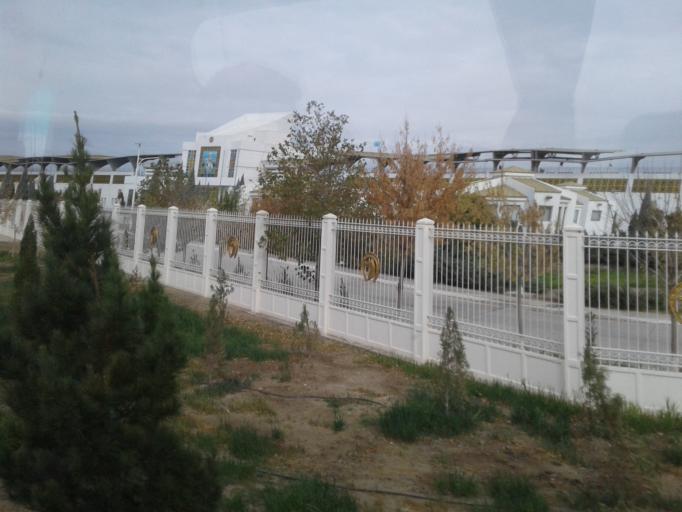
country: TM
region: Lebap
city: Turkmenabat
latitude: 38.9892
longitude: 63.5614
